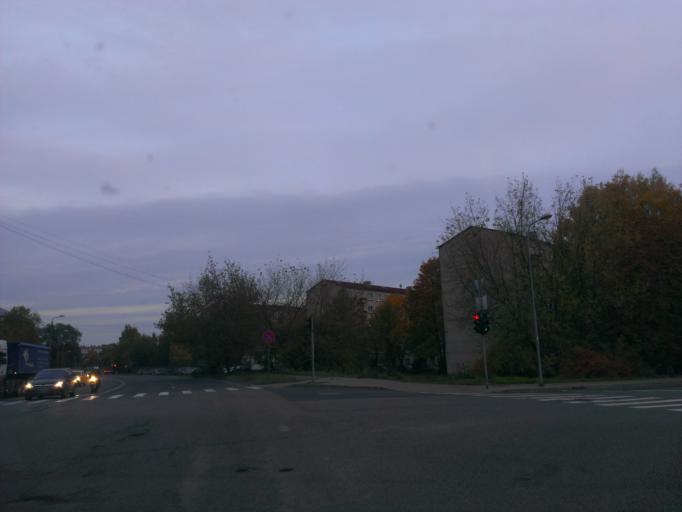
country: LV
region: Riga
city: Riga
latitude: 56.9728
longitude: 24.1296
